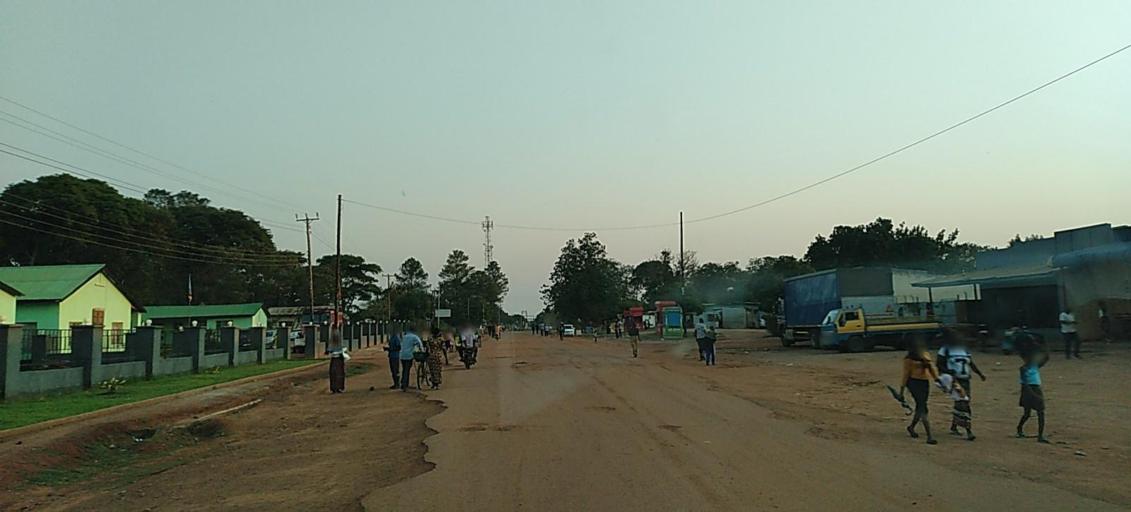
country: ZM
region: North-Western
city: Mwinilunga
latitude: -11.7362
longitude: 24.4309
